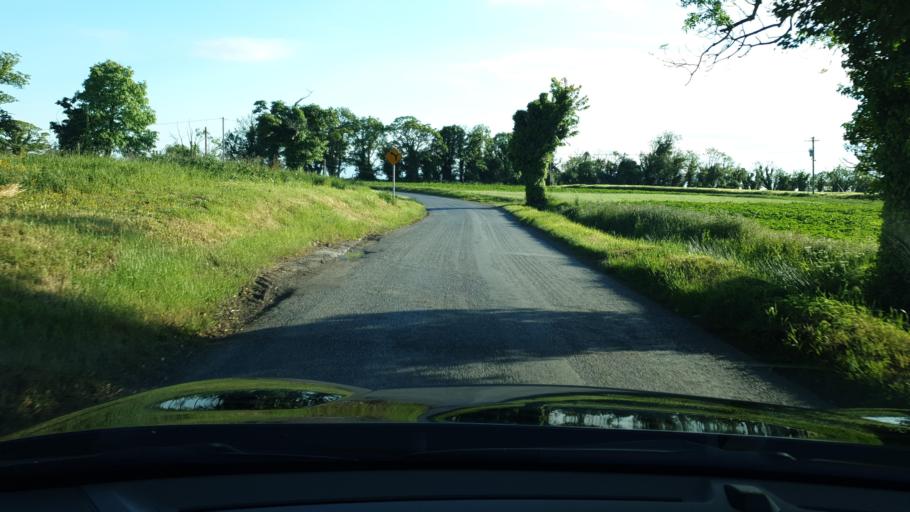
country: IE
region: Leinster
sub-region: Fingal County
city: Swords
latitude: 53.5049
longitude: -6.2395
